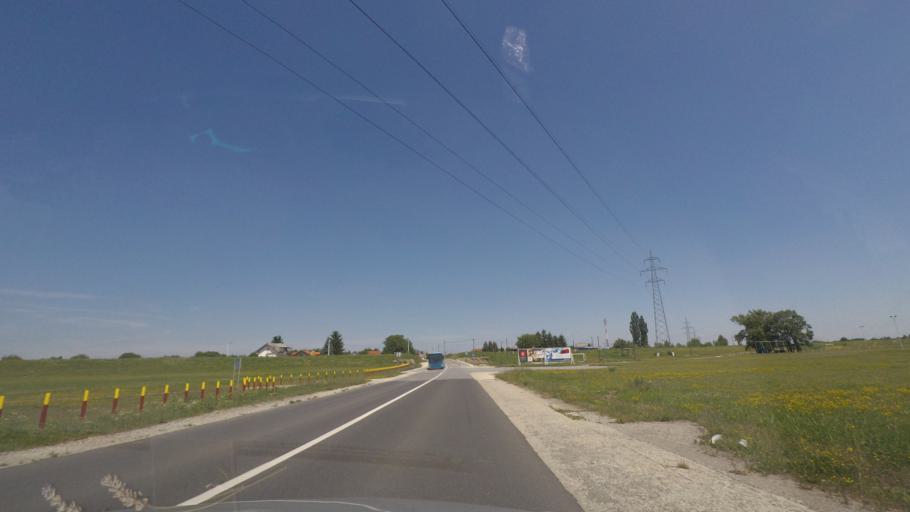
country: HR
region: Grad Zagreb
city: Zadvorsko
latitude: 45.7595
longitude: 15.9093
